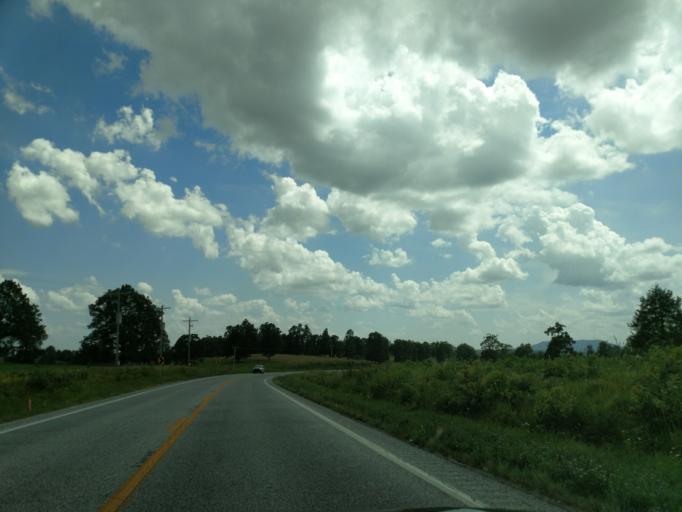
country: US
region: Arkansas
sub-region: Boone County
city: Harrison
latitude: 36.2061
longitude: -92.9338
